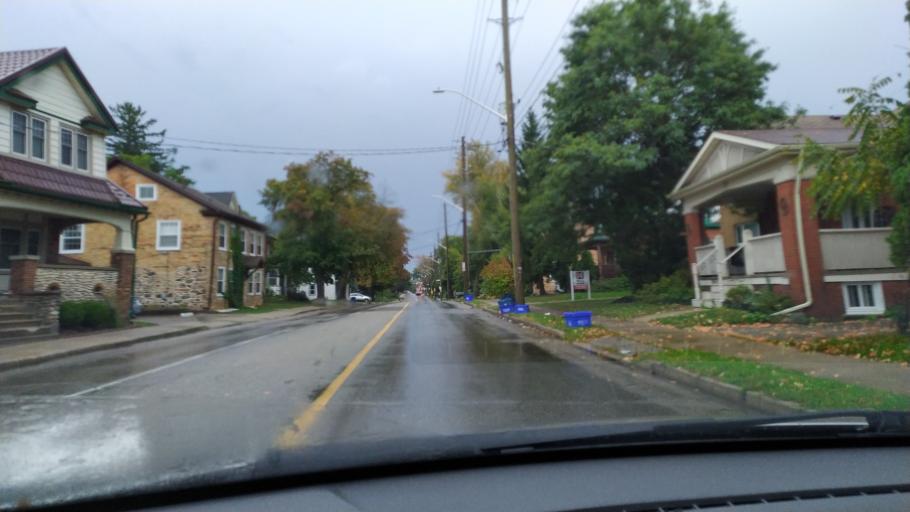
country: CA
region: Ontario
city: Waterloo
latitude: 43.4700
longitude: -80.5276
